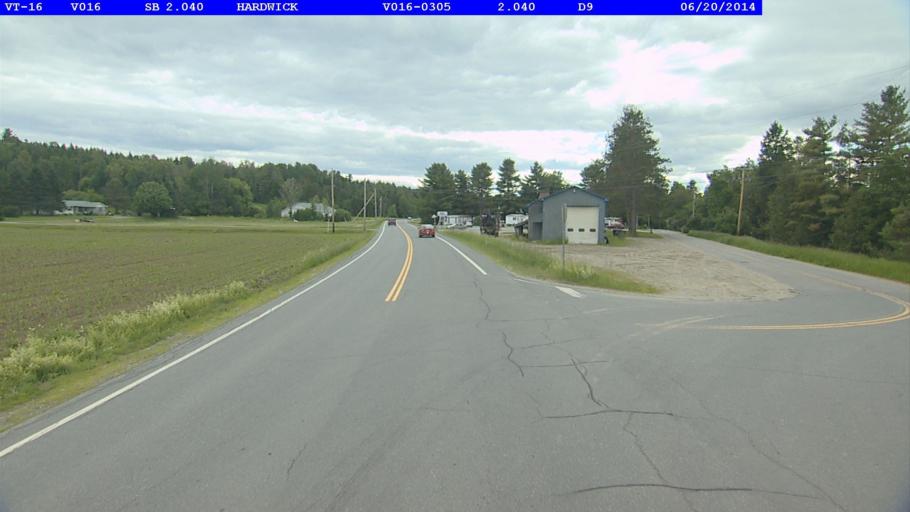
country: US
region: Vermont
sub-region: Caledonia County
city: Hardwick
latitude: 44.5213
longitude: -72.3006
